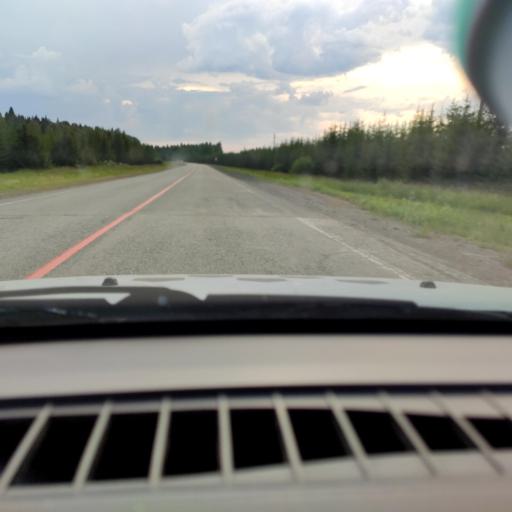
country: RU
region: Udmurtiya
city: Debesy
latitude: 57.6277
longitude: 53.7343
